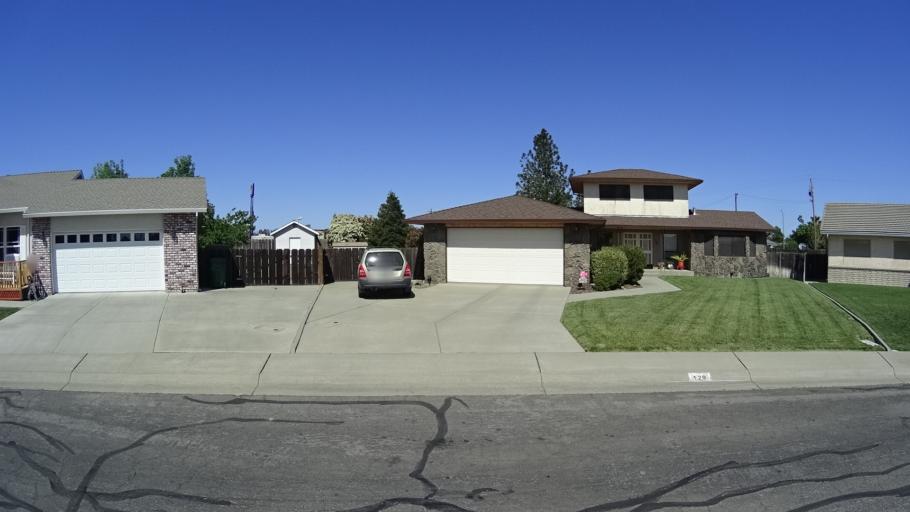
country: US
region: California
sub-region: Glenn County
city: Orland
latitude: 39.7541
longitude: -122.2038
